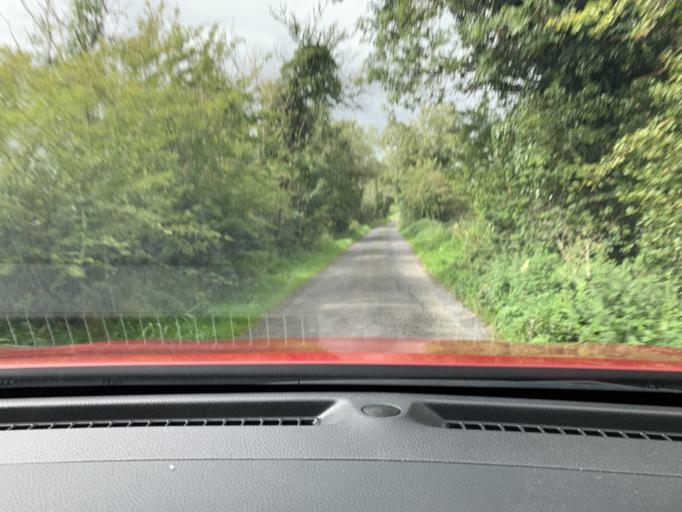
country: IE
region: Connaught
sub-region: Sligo
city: Collooney
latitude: 54.1567
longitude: -8.4274
